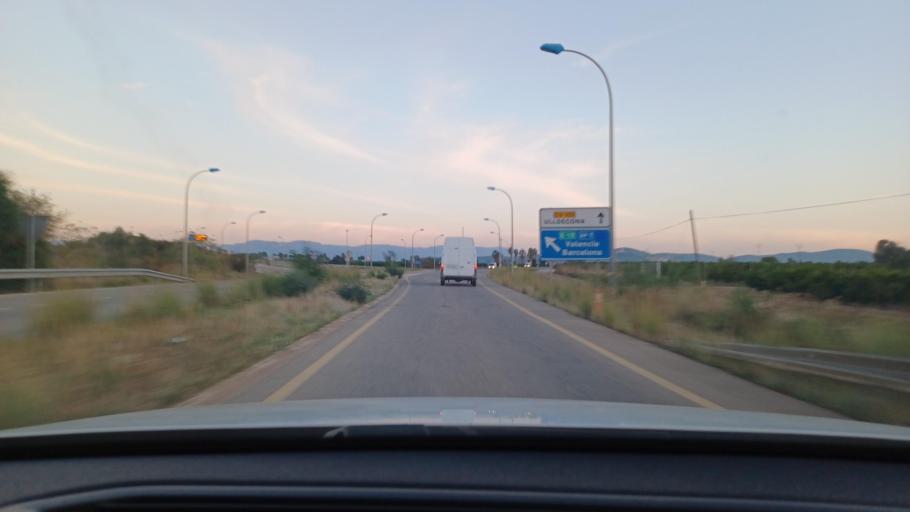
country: ES
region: Catalonia
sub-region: Provincia de Tarragona
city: Ulldecona
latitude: 40.5527
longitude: 0.4324
